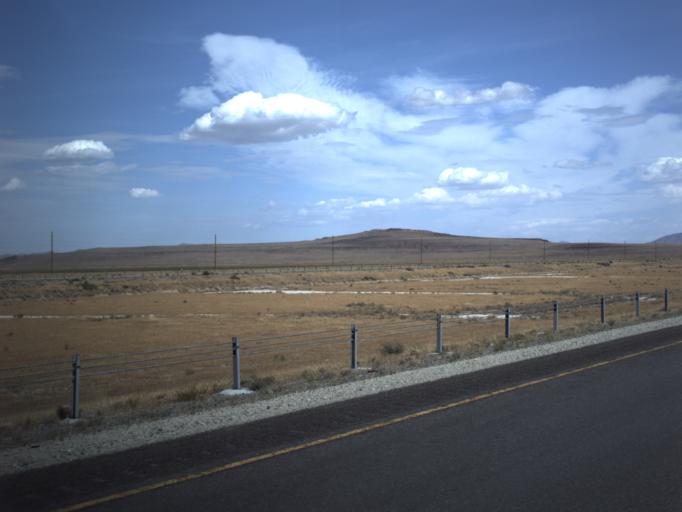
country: US
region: Utah
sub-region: Tooele County
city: Grantsville
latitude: 40.7257
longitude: -113.1928
